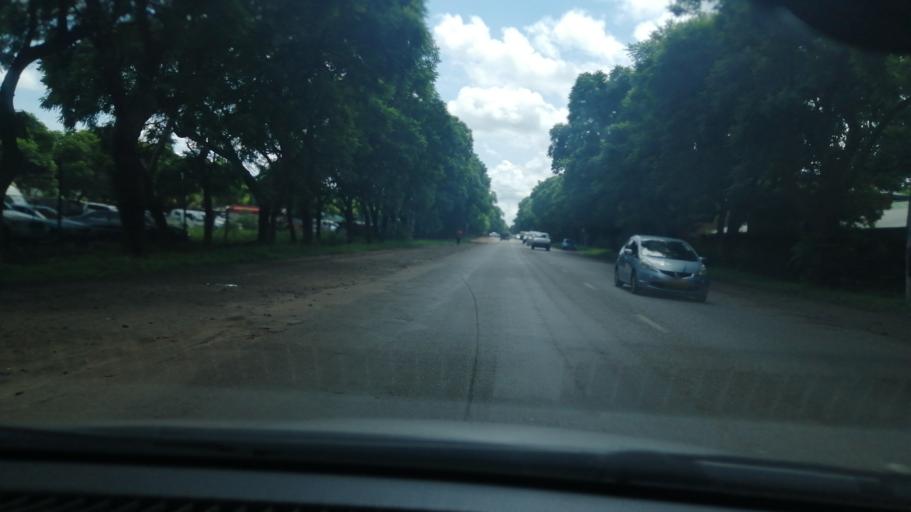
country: ZW
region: Harare
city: Harare
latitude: -17.8191
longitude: 31.0344
